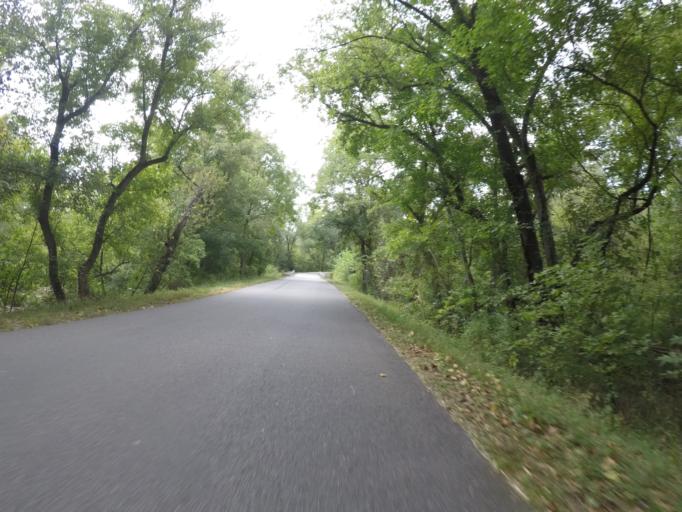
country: US
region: West Virginia
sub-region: Cabell County
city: Huntington
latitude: 38.4578
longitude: -82.4043
